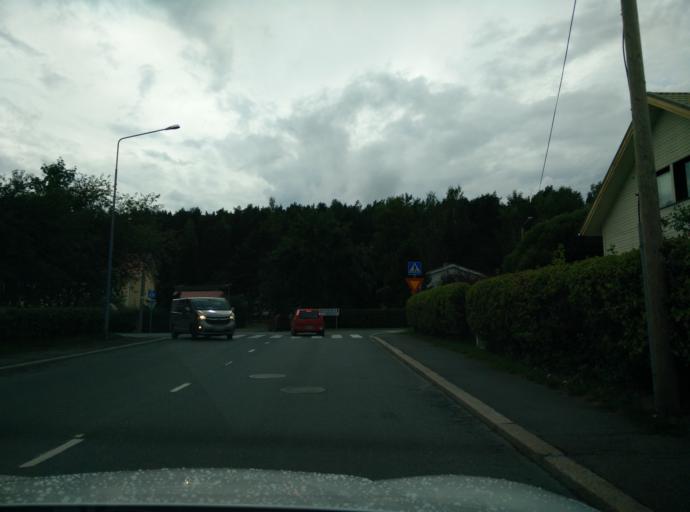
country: FI
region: Haeme
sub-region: Haemeenlinna
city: Haemeenlinna
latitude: 61.0000
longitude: 24.4268
